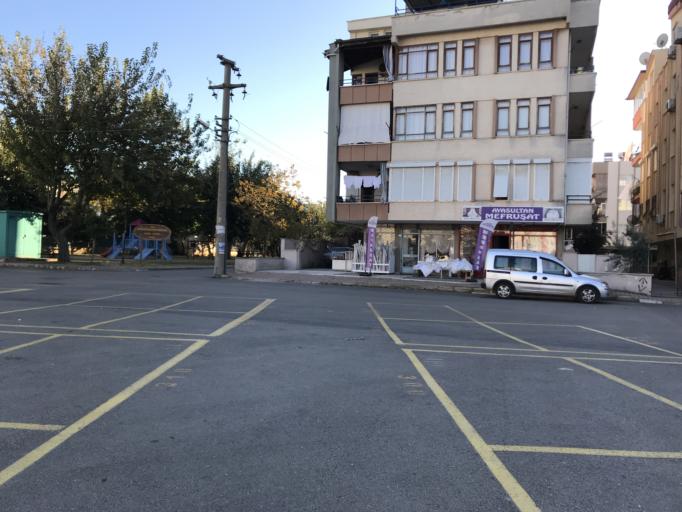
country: TR
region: Antalya
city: Antalya
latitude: 36.9027
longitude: 30.7079
